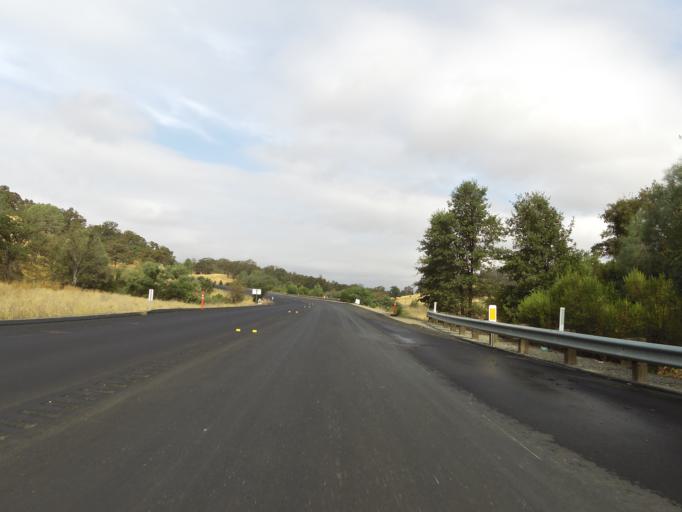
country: US
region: California
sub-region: Calaveras County
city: Angels Camp
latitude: 38.0366
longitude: -120.5095
